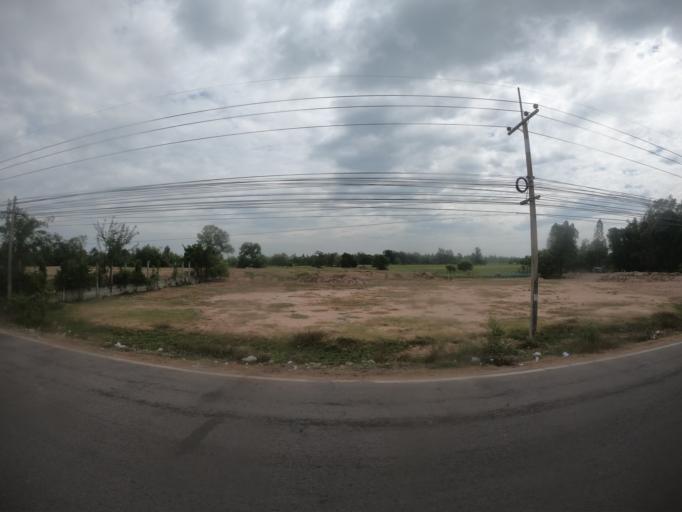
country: TH
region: Maha Sarakham
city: Kantharawichai
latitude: 16.2966
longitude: 103.2966
